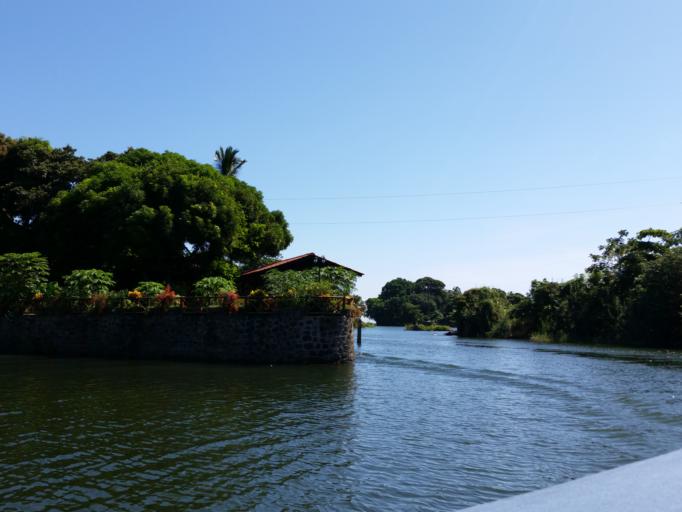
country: NI
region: Granada
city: Granada
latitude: 11.8771
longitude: -85.8959
